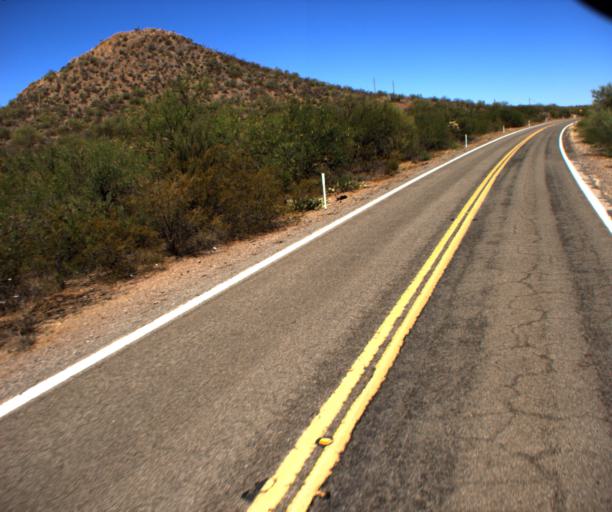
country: US
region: Arizona
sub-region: Pima County
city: Sells
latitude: 32.1710
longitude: -112.1501
